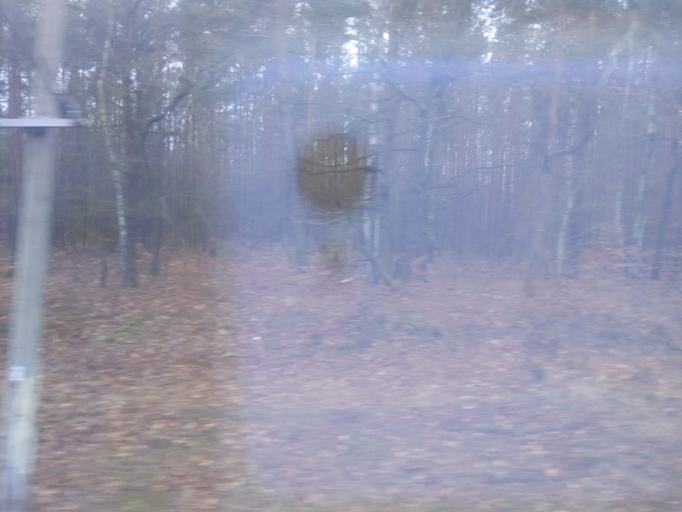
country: DE
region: Saxony
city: Albertstadt
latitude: 51.1069
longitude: 13.7888
